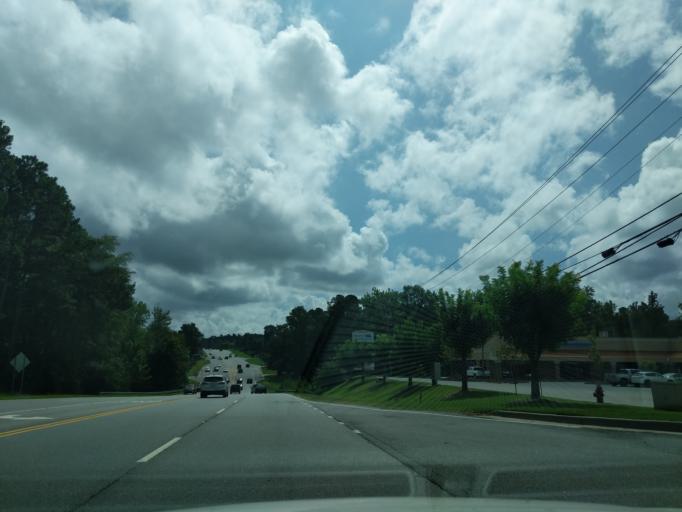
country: US
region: Georgia
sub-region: Columbia County
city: Evans
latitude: 33.5471
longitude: -82.1482
